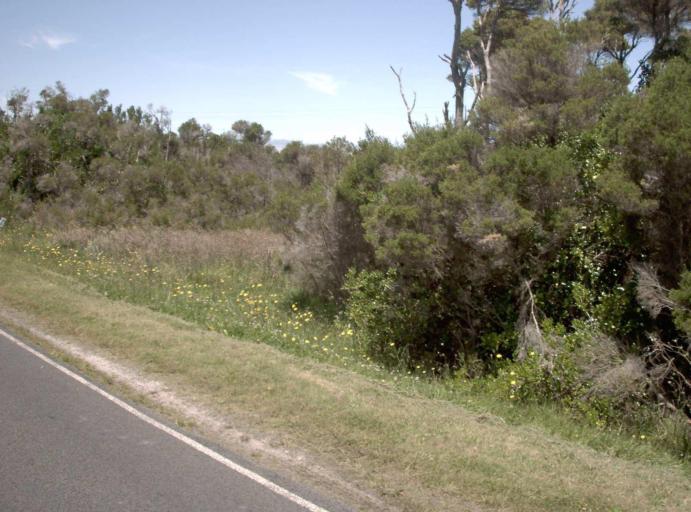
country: AU
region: Victoria
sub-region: Latrobe
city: Morwell
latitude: -38.7926
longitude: 146.1797
